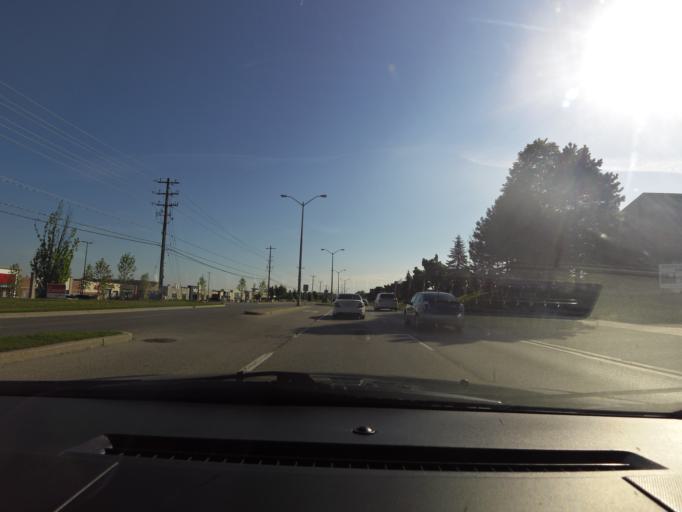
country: CA
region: Ontario
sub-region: Wellington County
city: Guelph
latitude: 43.5162
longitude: -80.2387
